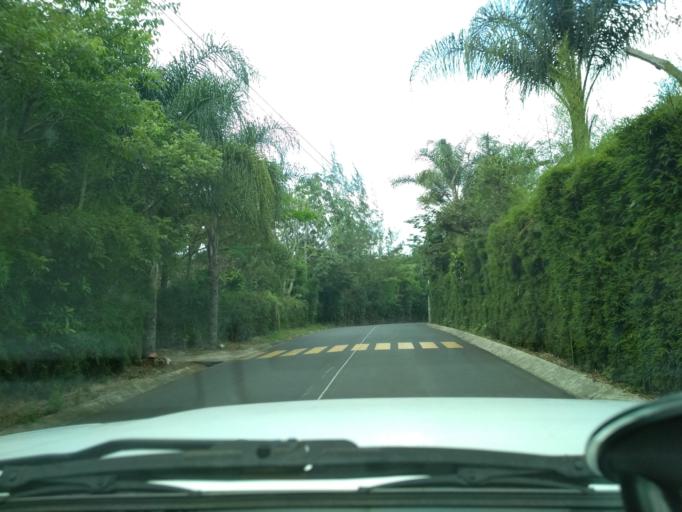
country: MX
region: Veracruz
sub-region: Cordoba
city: San Jose de Abajo [Unidad Habitacional]
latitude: 18.9232
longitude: -96.9580
